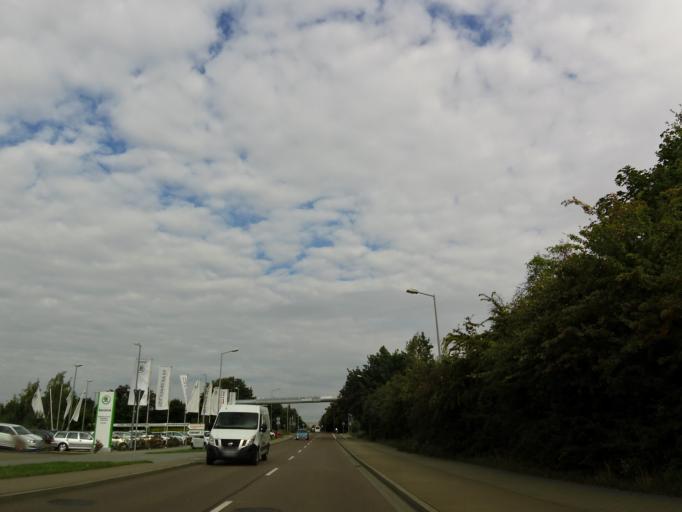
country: DE
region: Saxony
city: Leipzig
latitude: 51.3111
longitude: 12.3092
